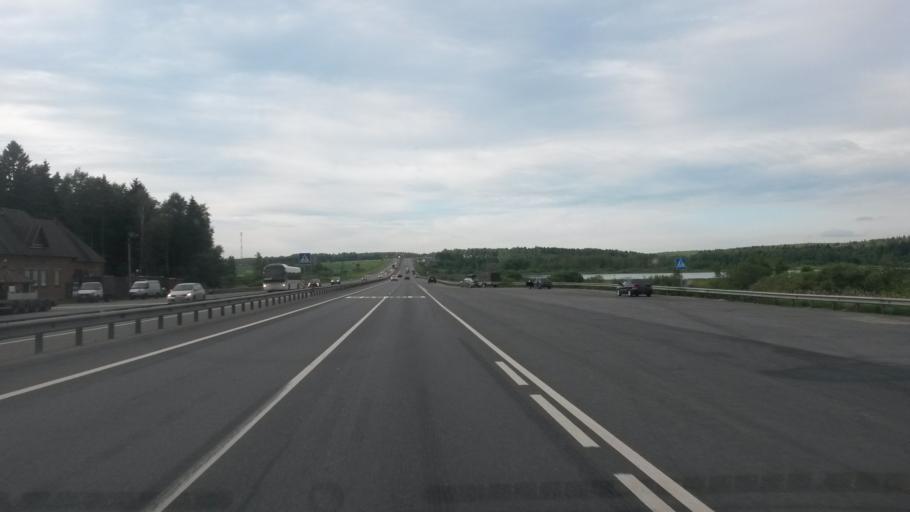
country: RU
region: Moskovskaya
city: Svatkovo
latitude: 56.3264
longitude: 38.2534
